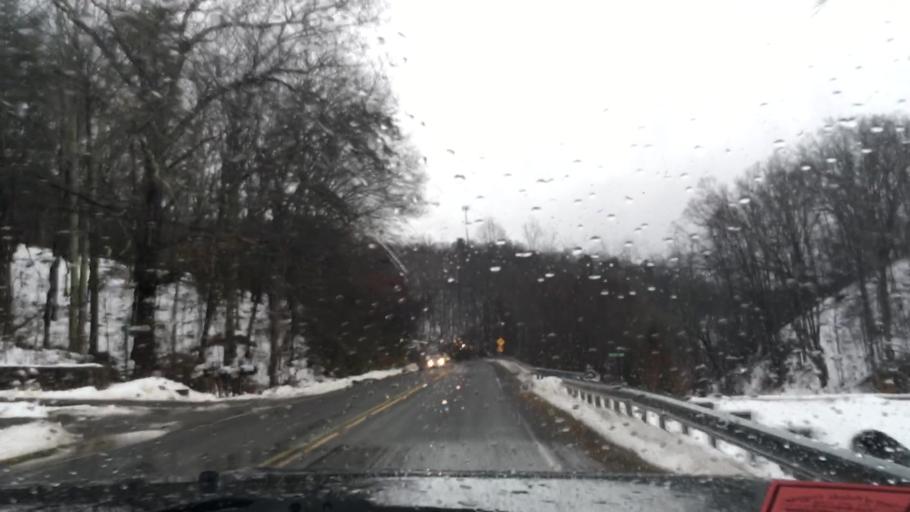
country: US
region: Virginia
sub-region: Pulaski County
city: Dublin
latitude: 37.0102
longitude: -80.6887
